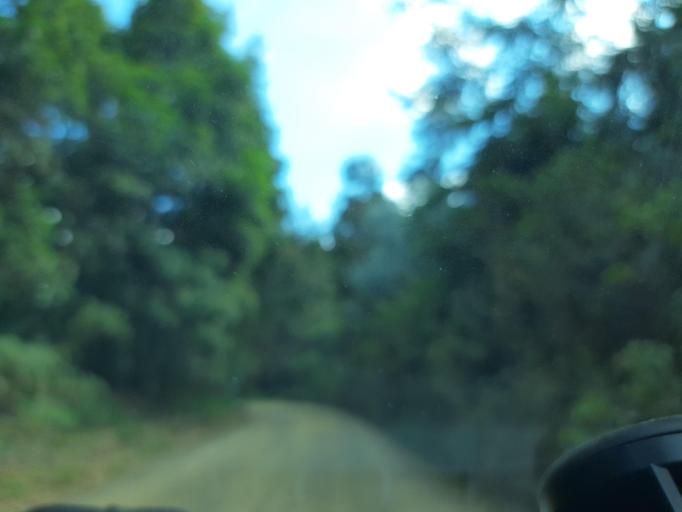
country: CO
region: Boyaca
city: Raquira
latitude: 5.5364
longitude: -73.6594
